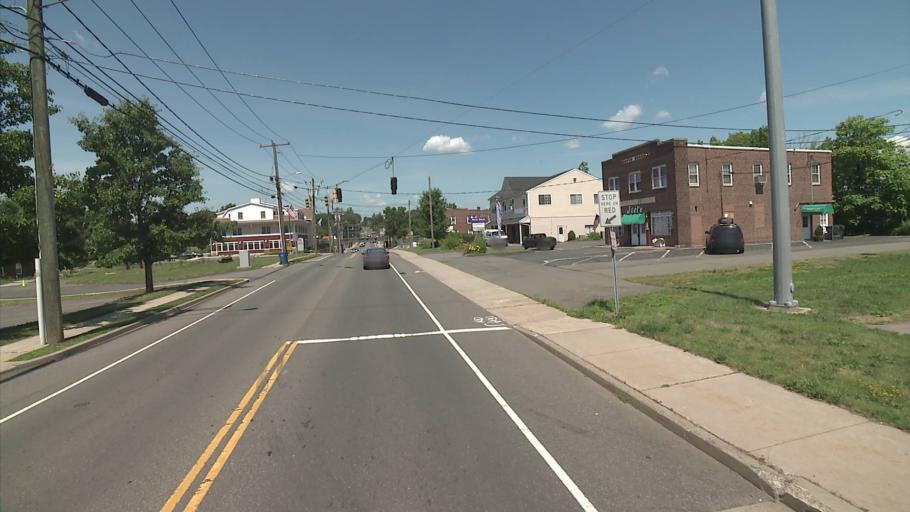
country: US
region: Connecticut
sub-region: Hartford County
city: Kensington
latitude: 41.6337
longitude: -72.7645
